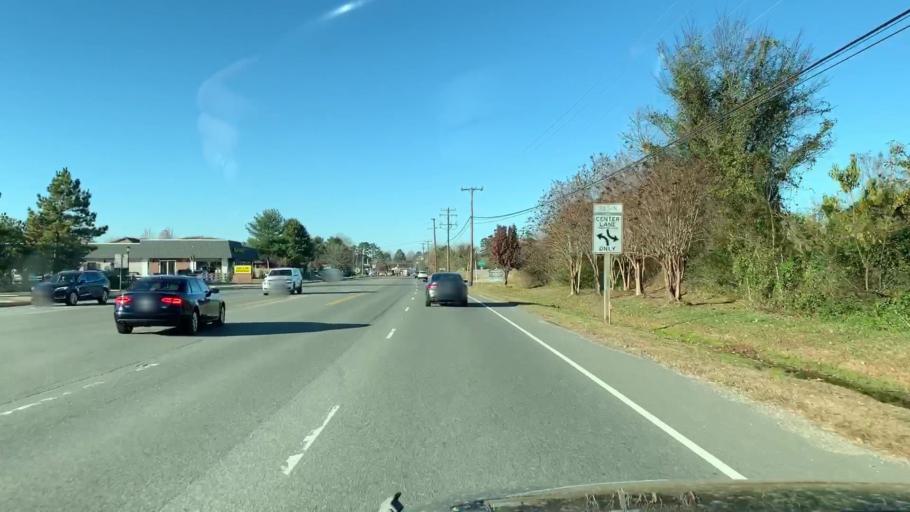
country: US
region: Virginia
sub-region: James City County
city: Williamsburg
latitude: 37.3590
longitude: -76.7646
